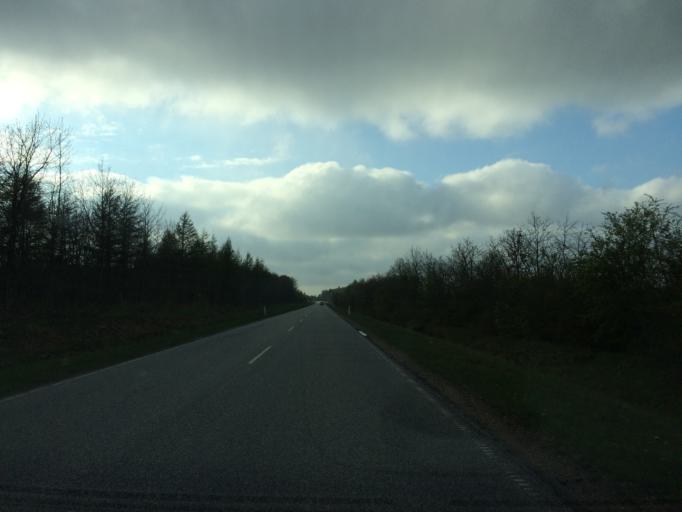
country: DK
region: Central Jutland
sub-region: Viborg Kommune
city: Karup
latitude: 56.3319
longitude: 9.0996
